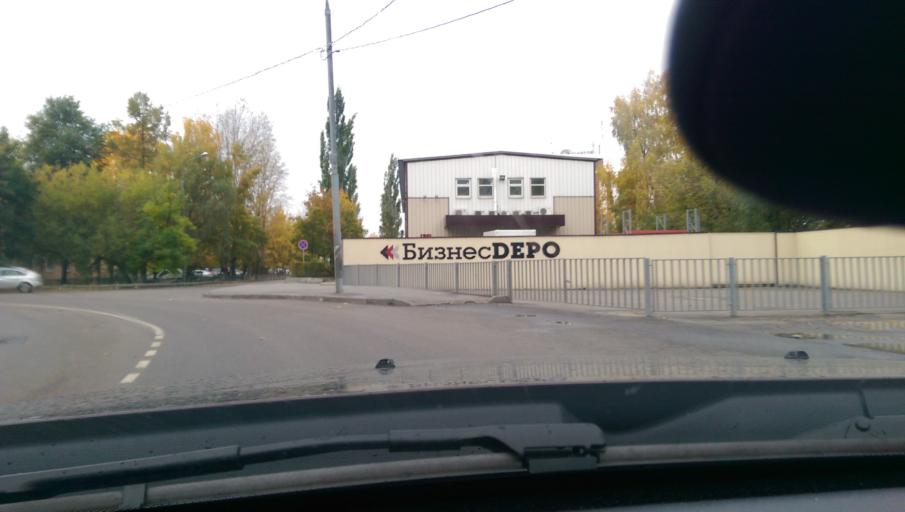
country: RU
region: Moscow
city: Altuf'yevskiy
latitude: 55.8910
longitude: 37.5796
